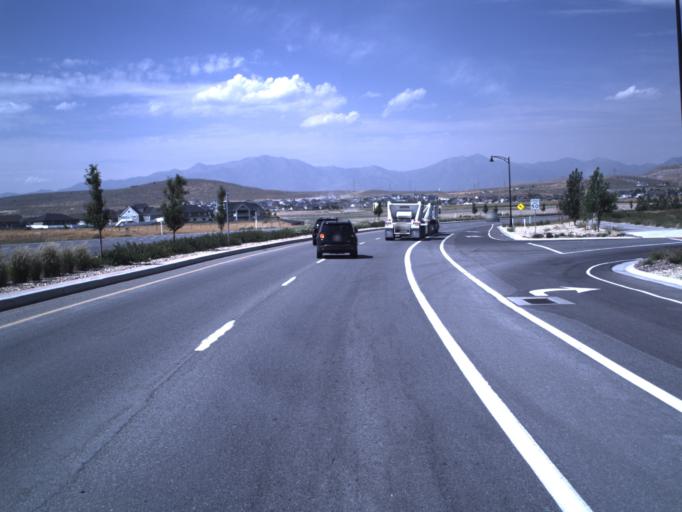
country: US
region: Utah
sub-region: Utah County
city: Saratoga Springs
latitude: 40.3729
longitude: -111.9182
